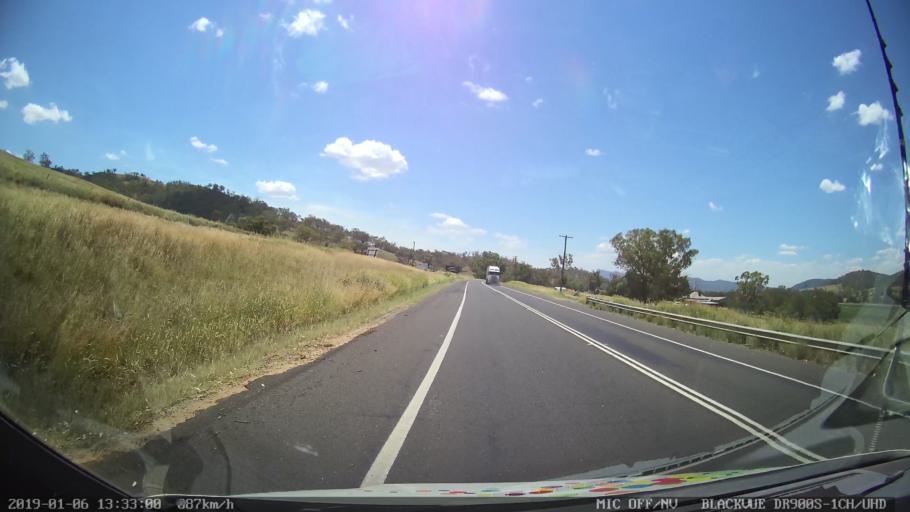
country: AU
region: New South Wales
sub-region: Tamworth Municipality
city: East Tamworth
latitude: -31.1040
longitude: 151.0021
